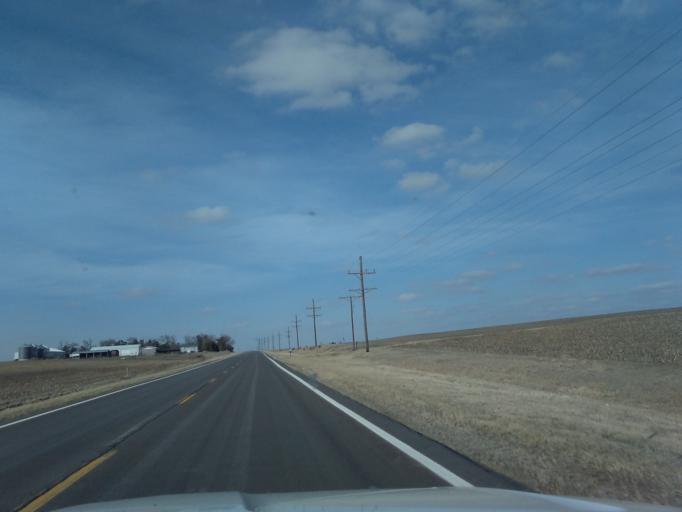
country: US
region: Nebraska
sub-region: Gage County
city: Beatrice
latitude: 40.1683
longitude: -96.9352
